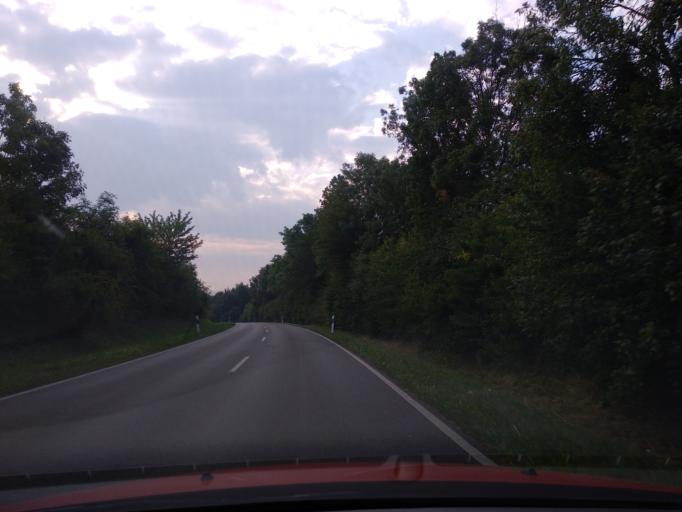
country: DE
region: Hesse
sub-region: Regierungsbezirk Kassel
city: Calden
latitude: 51.3719
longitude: 9.3880
